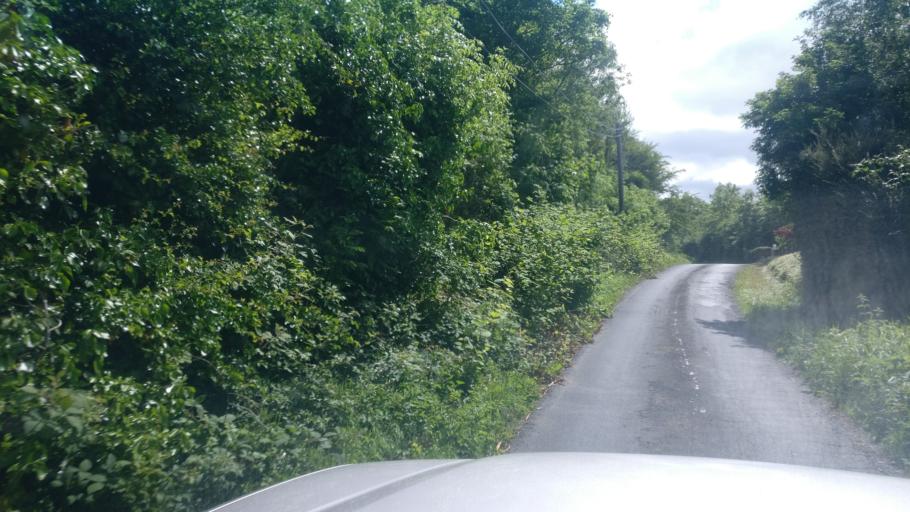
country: IE
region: Connaught
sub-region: County Galway
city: Gort
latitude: 53.1324
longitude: -8.7084
